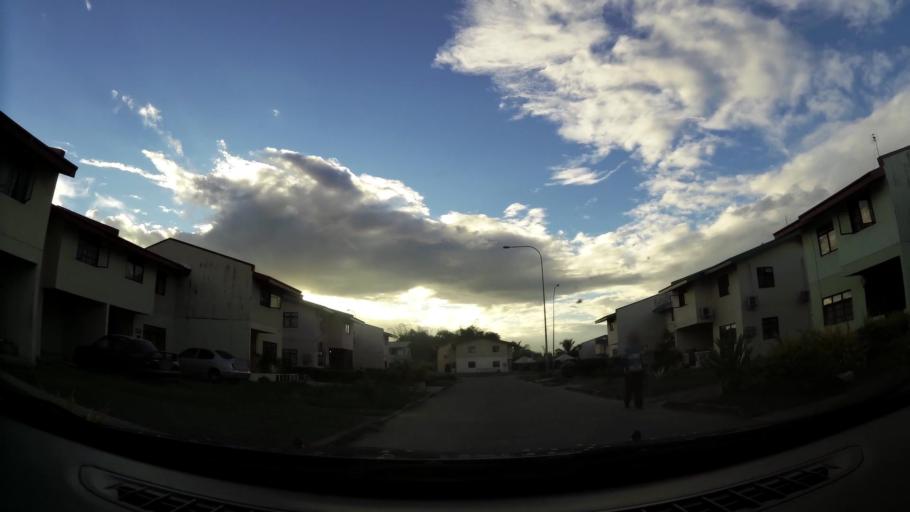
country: TT
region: Tunapuna/Piarco
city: Arouca
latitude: 10.6177
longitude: -61.3549
